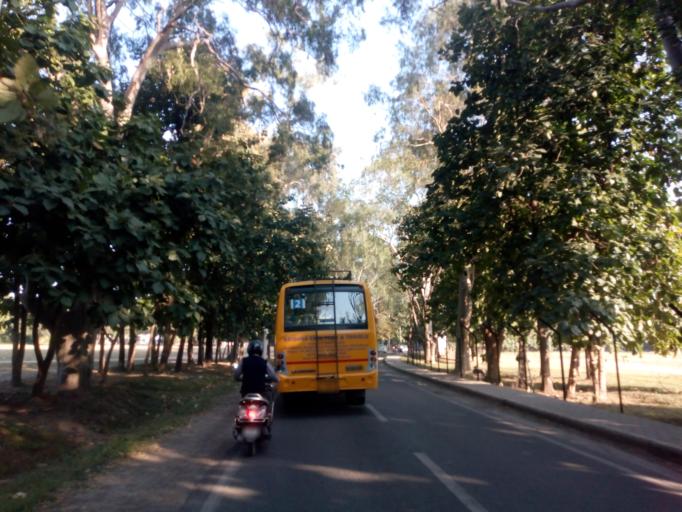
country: IN
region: Uttarakhand
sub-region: Dehradun
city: Dehradun
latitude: 30.3522
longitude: 78.0319
